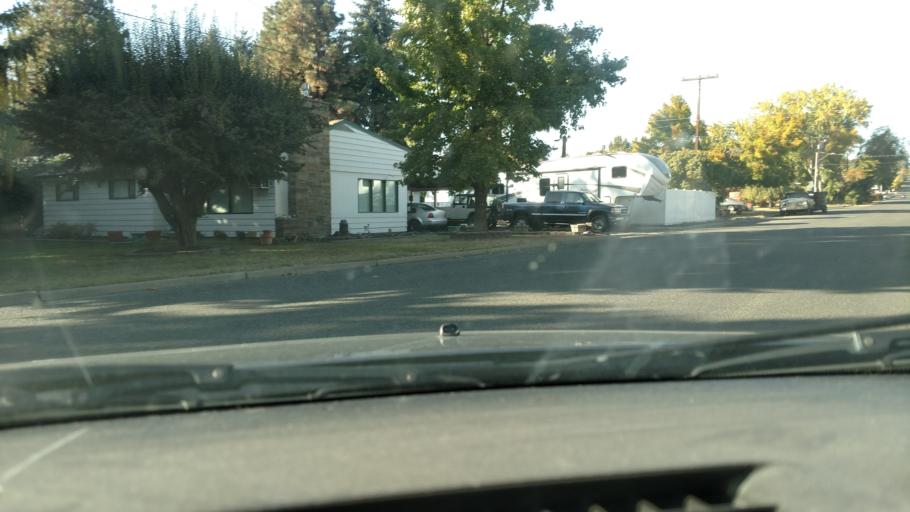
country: US
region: Washington
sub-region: Kittitas County
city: Ellensburg
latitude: 46.9886
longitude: -120.5330
